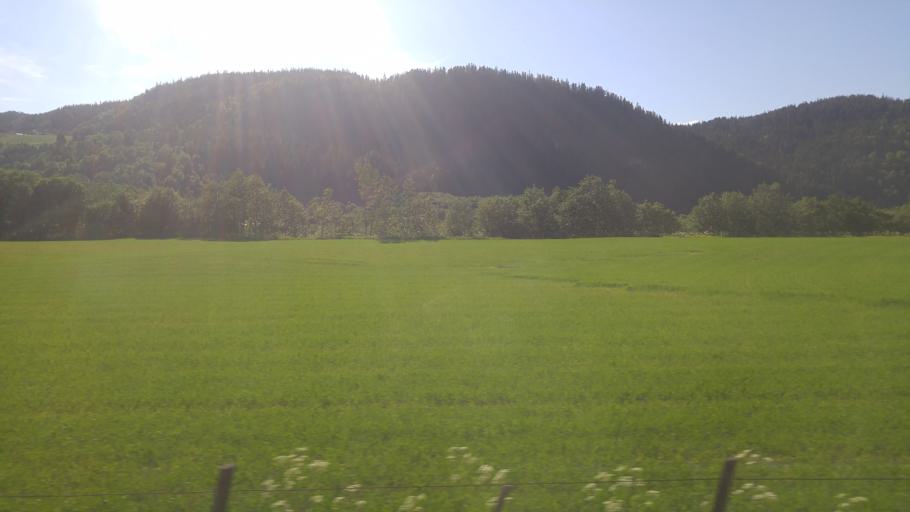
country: NO
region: Sor-Trondelag
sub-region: Melhus
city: Lundamo
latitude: 63.1827
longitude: 10.3083
